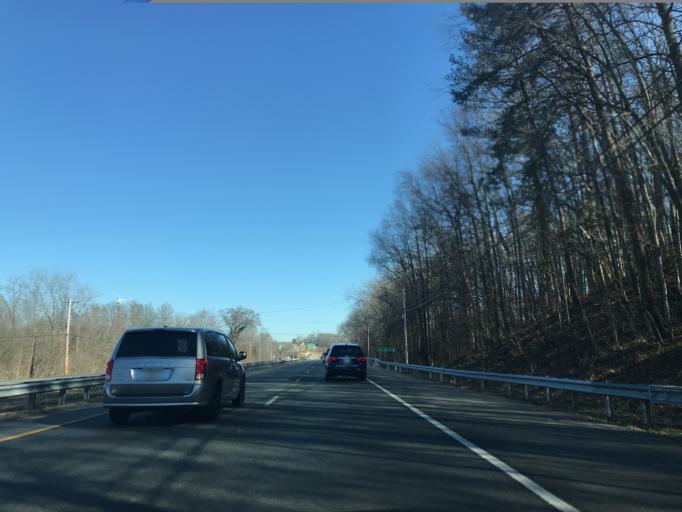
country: US
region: Maryland
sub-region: Prince George's County
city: Accokeek
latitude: 38.6521
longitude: -76.9827
